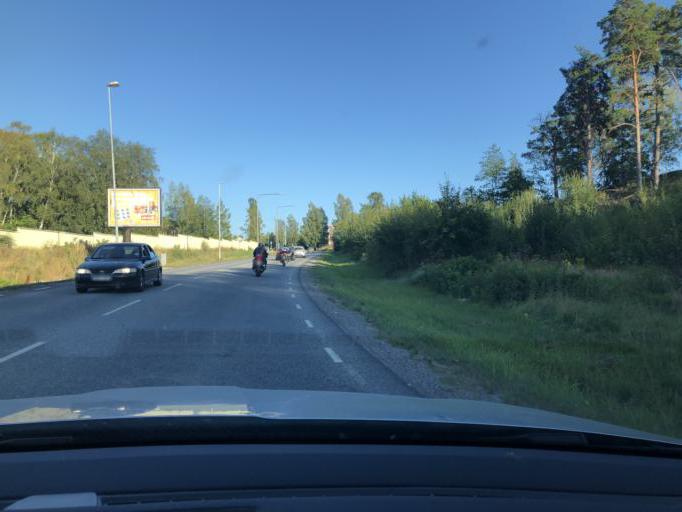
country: SE
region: Stockholm
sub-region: Sodertalje Kommun
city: Soedertaelje
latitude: 59.1843
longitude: 17.5919
